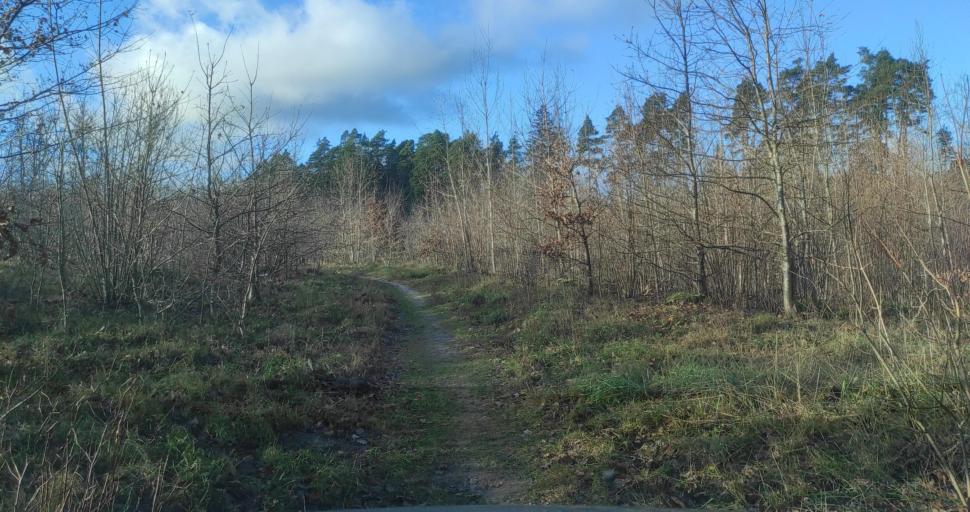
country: LV
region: Kuldigas Rajons
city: Kuldiga
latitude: 56.9619
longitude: 21.9280
